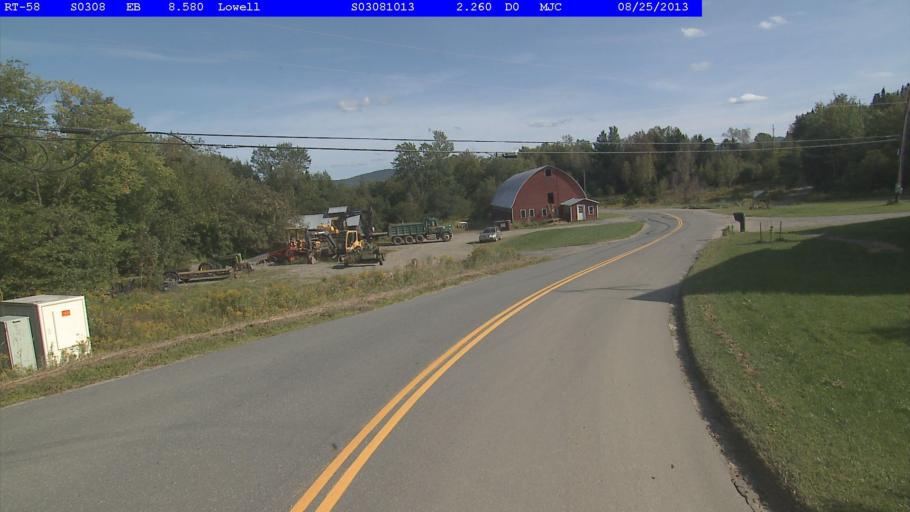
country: US
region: Vermont
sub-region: Lamoille County
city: Hyde Park
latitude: 44.8167
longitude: -72.4722
